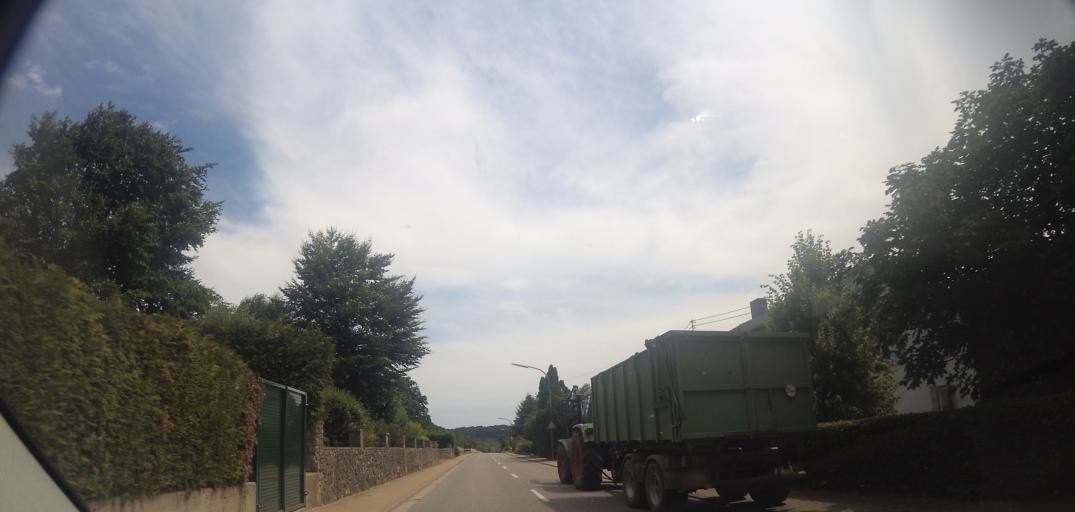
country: DE
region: Saarland
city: Merzig
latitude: 49.4219
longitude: 6.5763
